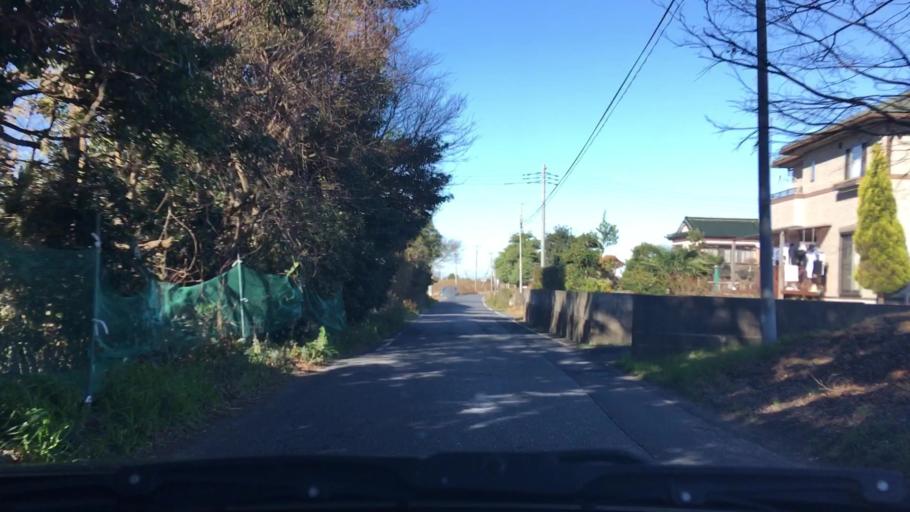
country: JP
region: Chiba
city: Omigawa
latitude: 35.8733
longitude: 140.6359
